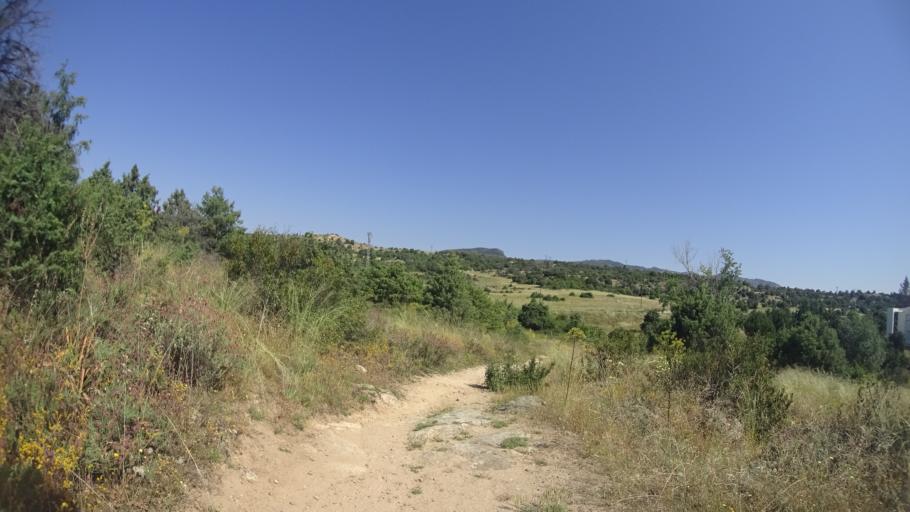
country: ES
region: Madrid
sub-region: Provincia de Madrid
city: Hoyo de Manzanares
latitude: 40.6031
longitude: -3.9078
